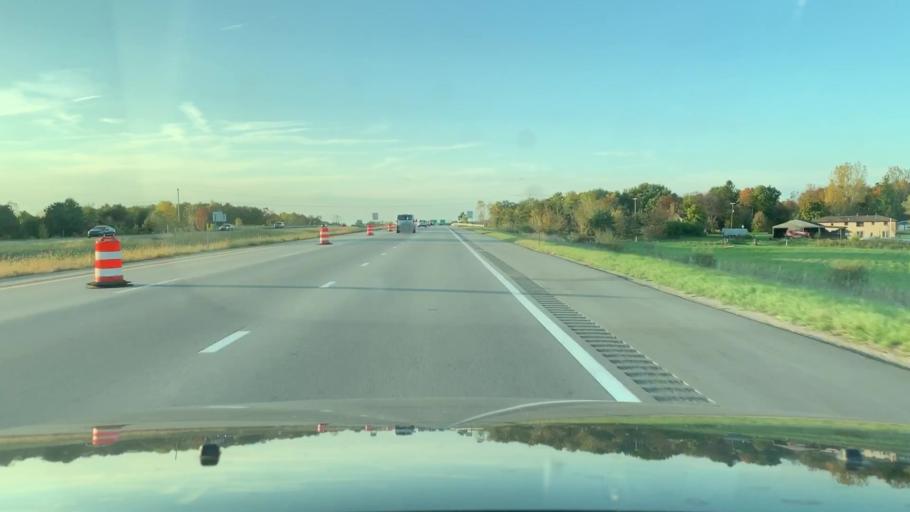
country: US
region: Michigan
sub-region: Ottawa County
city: Hudsonville
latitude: 42.8537
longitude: -85.8113
